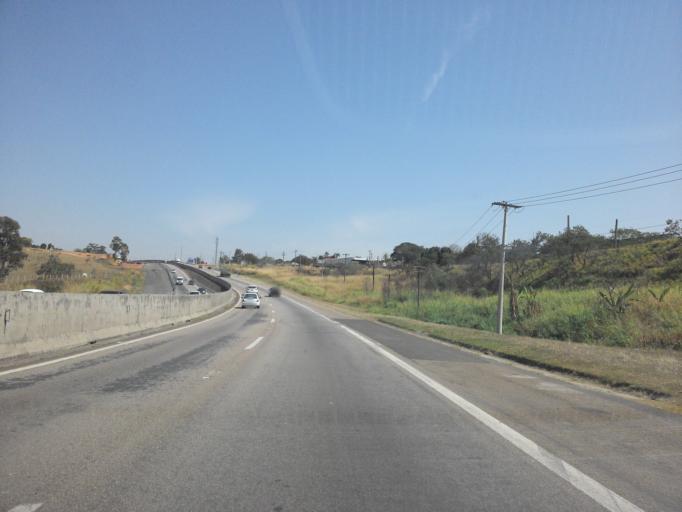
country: BR
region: Sao Paulo
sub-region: Hortolandia
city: Hortolandia
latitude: -22.8853
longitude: -47.1525
